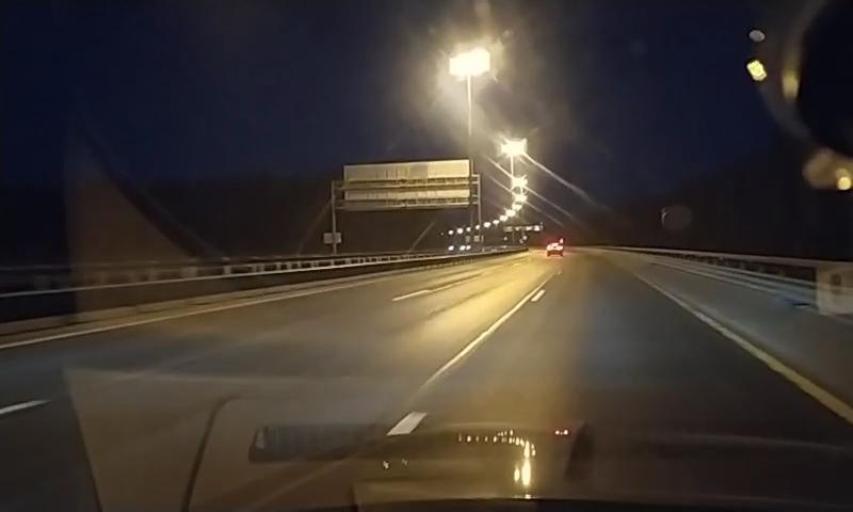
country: RU
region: St.-Petersburg
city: Pesochnyy
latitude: 60.0717
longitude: 30.1353
